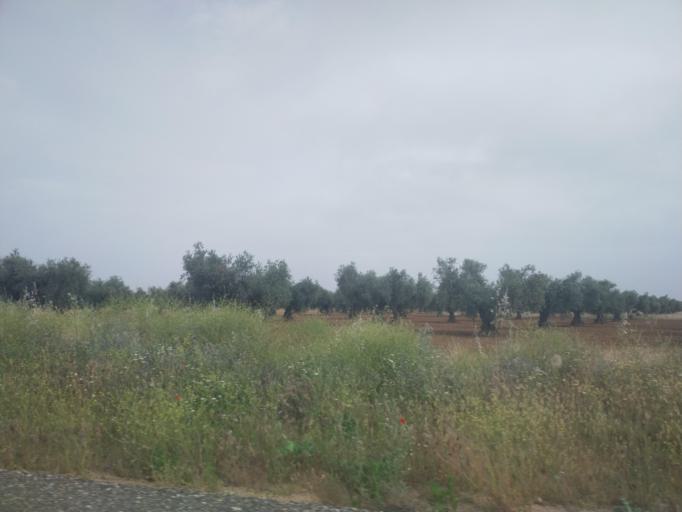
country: ES
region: Castille-La Mancha
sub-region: Province of Toledo
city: Polan
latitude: 39.7914
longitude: -4.1495
